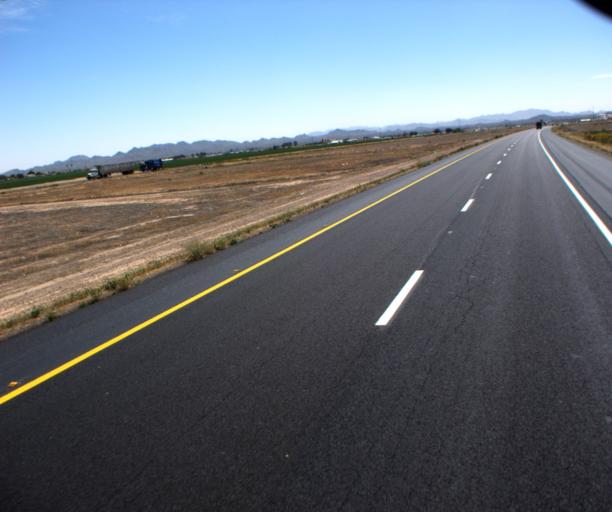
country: US
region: Arizona
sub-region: Maricopa County
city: Buckeye
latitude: 33.3864
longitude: -112.6268
